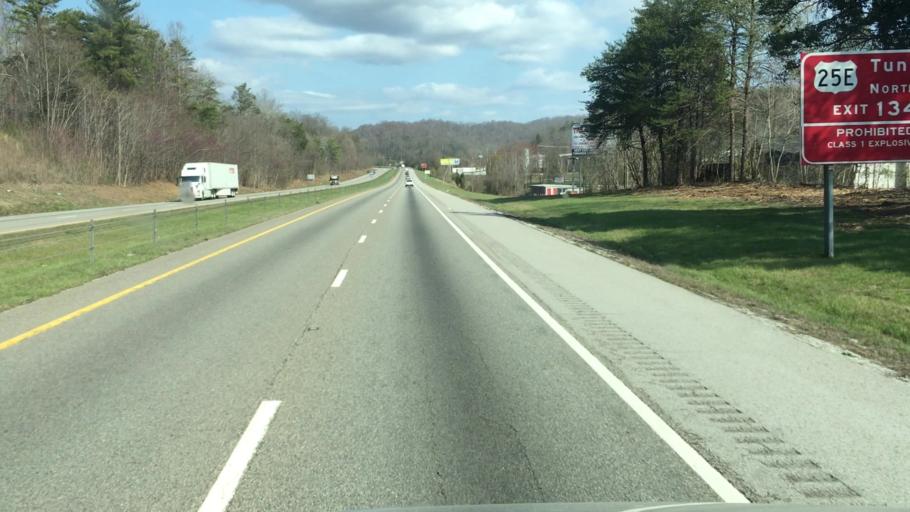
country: US
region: Tennessee
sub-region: Anderson County
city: Rocky Top
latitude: 36.2529
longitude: -84.1836
